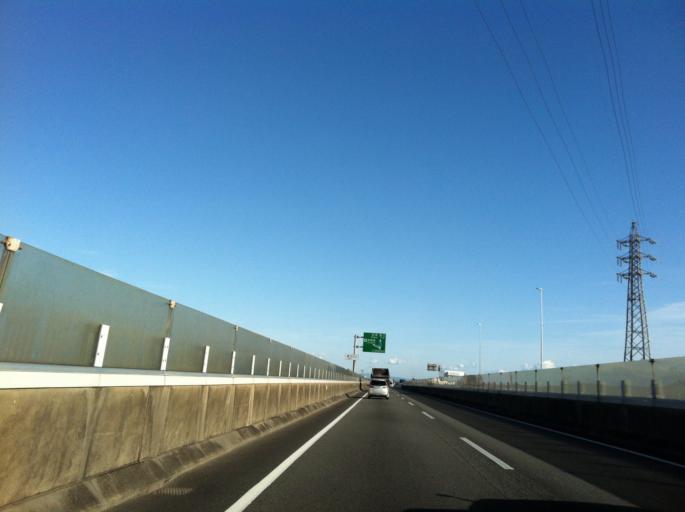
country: JP
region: Shizuoka
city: Shizuoka-shi
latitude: 35.0082
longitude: 138.4170
